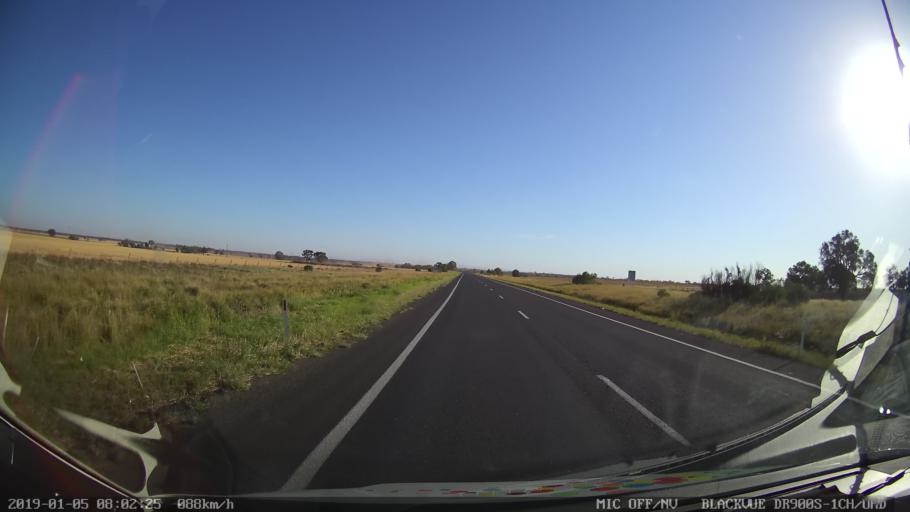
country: AU
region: New South Wales
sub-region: Gilgandra
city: Gilgandra
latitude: -31.6761
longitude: 148.7109
